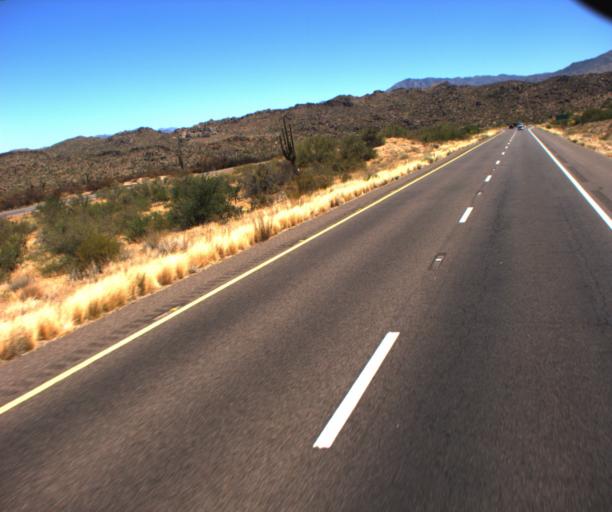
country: US
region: Arizona
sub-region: Maricopa County
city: Rio Verde
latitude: 33.6754
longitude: -111.5053
